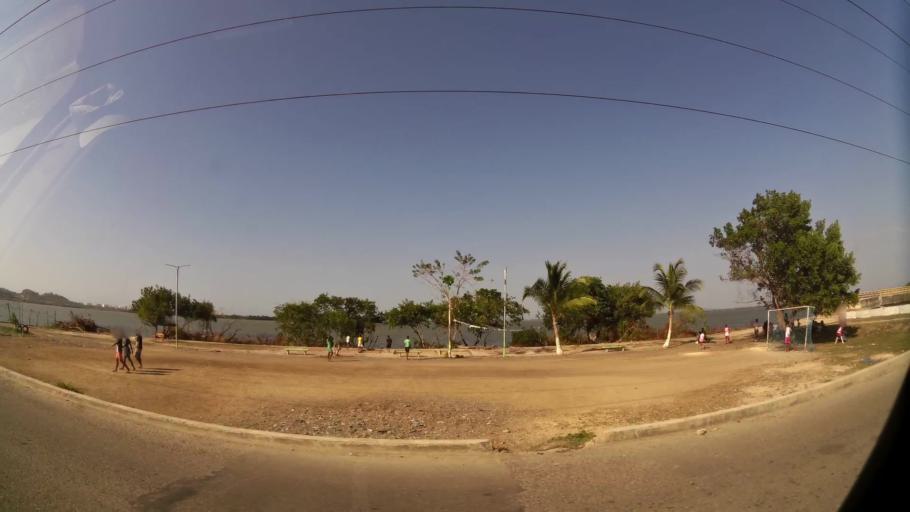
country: CO
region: Bolivar
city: Cartagena
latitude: 10.4149
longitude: -75.5019
